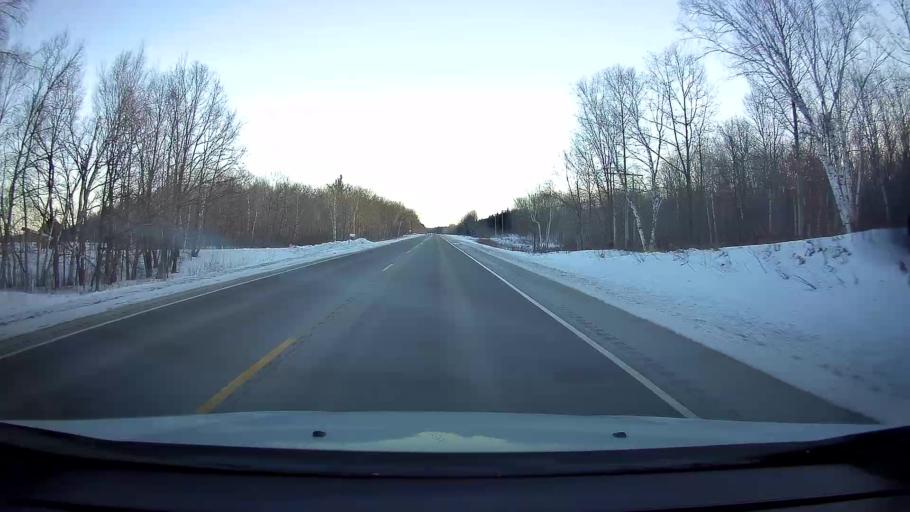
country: US
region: Wisconsin
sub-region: Washburn County
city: Shell Lake
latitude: 45.6975
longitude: -91.9610
